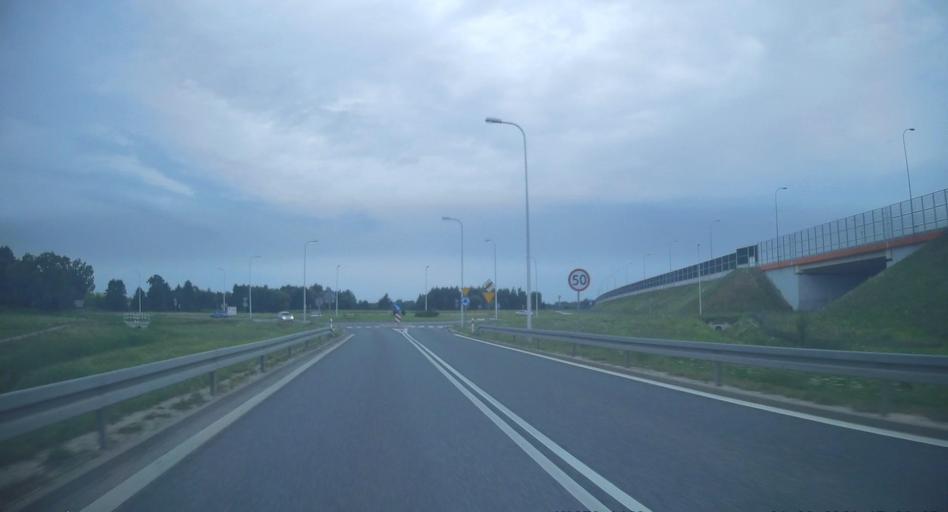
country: PL
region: Lesser Poland Voivodeship
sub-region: Powiat tarnowski
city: Wierzchoslawice
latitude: 50.0122
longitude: 20.8668
